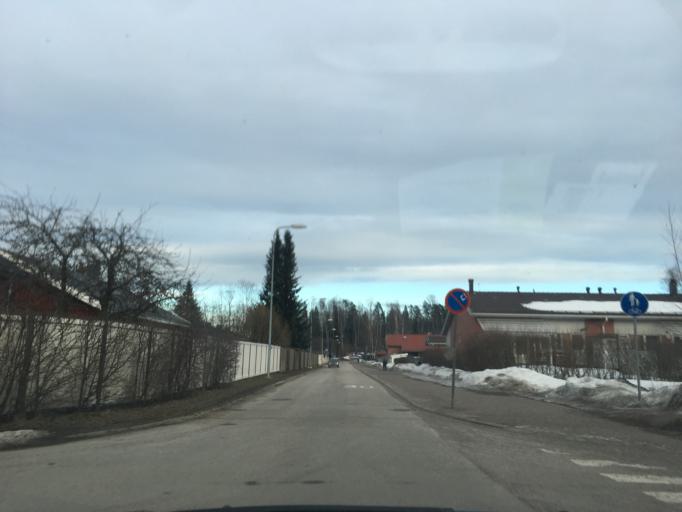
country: FI
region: Uusimaa
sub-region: Helsinki
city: Vantaa
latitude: 60.2669
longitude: 25.0929
